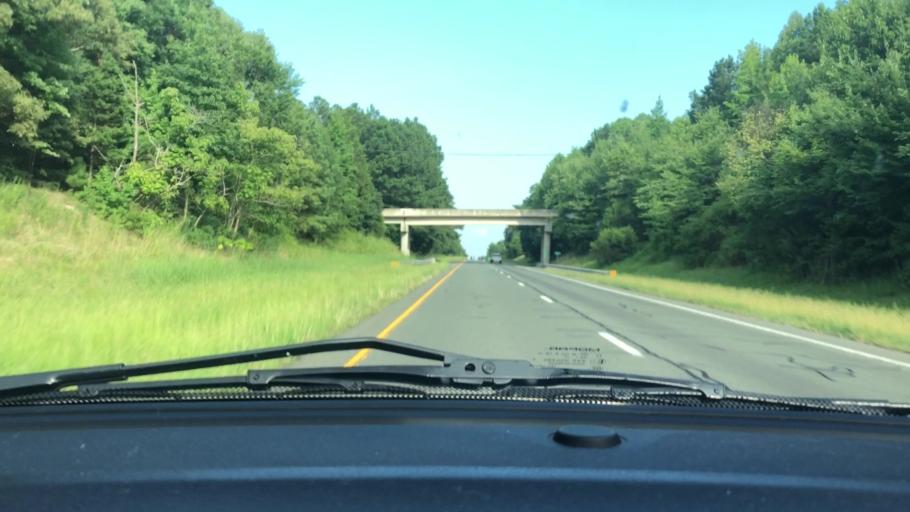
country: US
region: North Carolina
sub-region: Chatham County
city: Siler City
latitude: 35.7782
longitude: -79.5042
